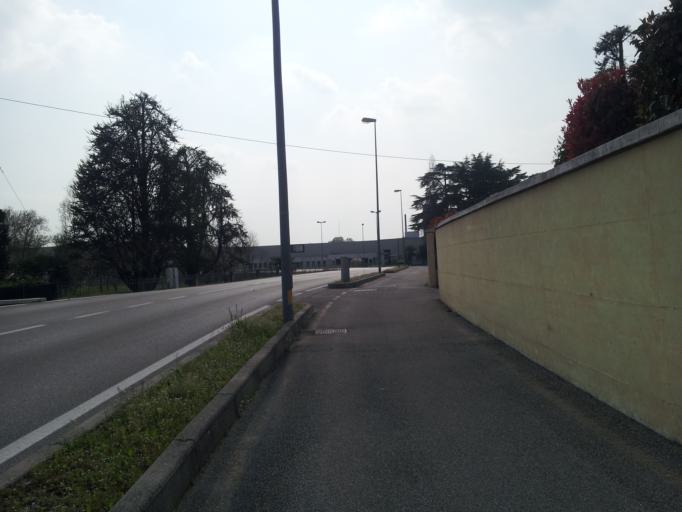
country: IT
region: Friuli Venezia Giulia
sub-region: Provincia di Pordenone
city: Pasiano
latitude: 45.8561
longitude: 12.6274
